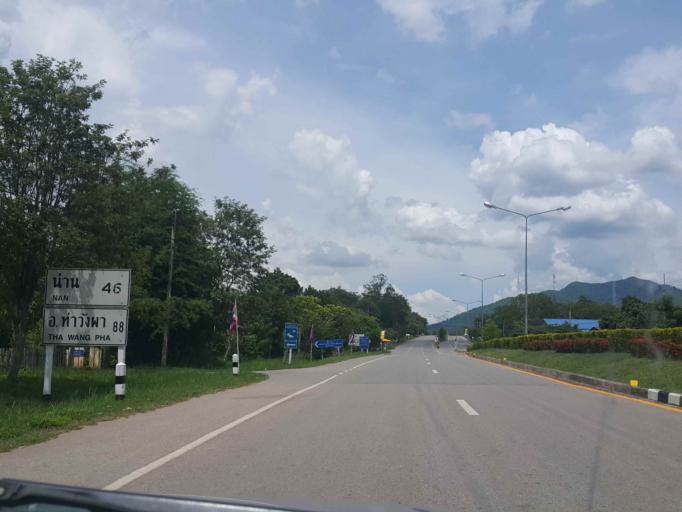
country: TH
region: Nan
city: Ban Luang
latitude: 18.8501
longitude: 100.4344
